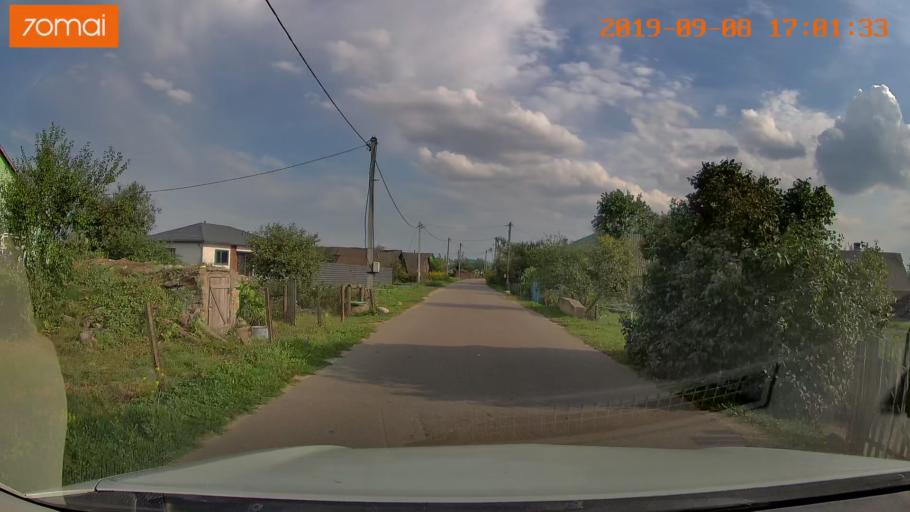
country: BY
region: Grodnenskaya
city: Hrodna
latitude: 53.7098
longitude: 23.9355
